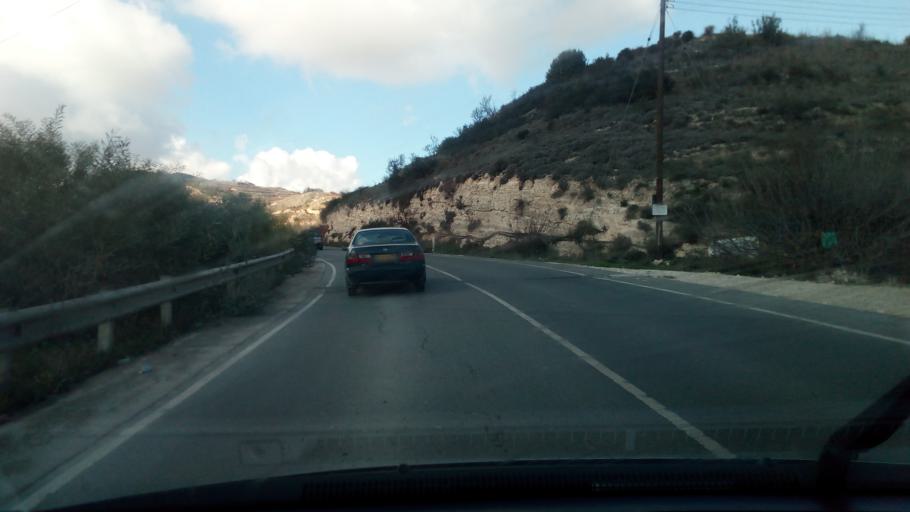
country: CY
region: Pafos
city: Tala
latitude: 34.8706
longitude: 32.4802
